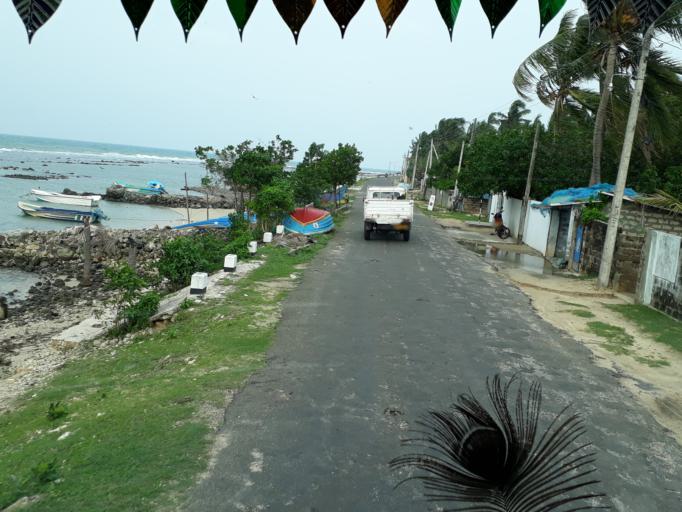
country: LK
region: Northern Province
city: Point Pedro
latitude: 9.8334
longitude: 80.2048
